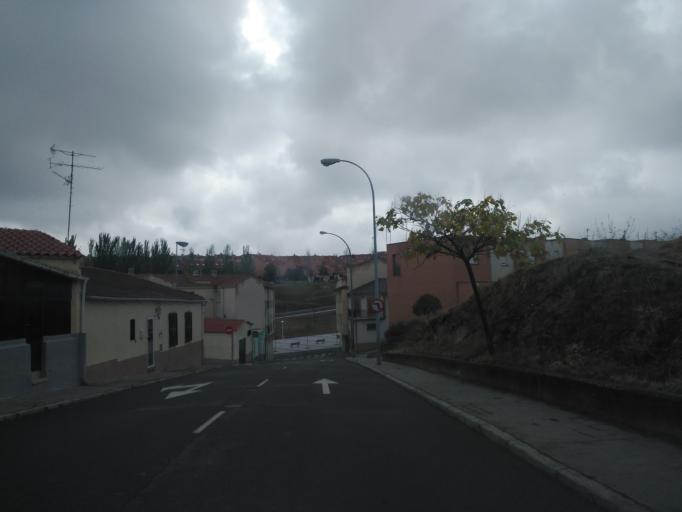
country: ES
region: Castille and Leon
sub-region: Provincia de Salamanca
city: Salamanca
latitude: 40.9528
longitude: -5.6830
